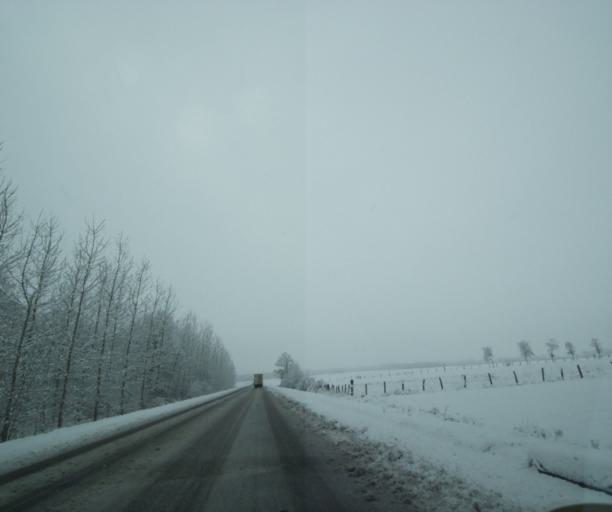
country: FR
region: Champagne-Ardenne
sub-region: Departement de la Haute-Marne
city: Saint-Dizier
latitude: 48.5997
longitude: 4.8968
